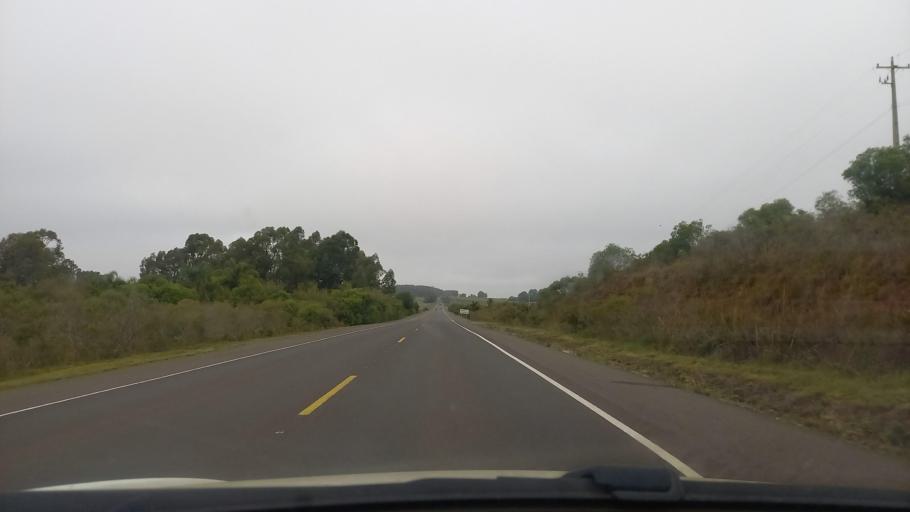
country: BR
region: Rio Grande do Sul
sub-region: Rosario Do Sul
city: Rosario do Sul
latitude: -30.3105
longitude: -54.9960
